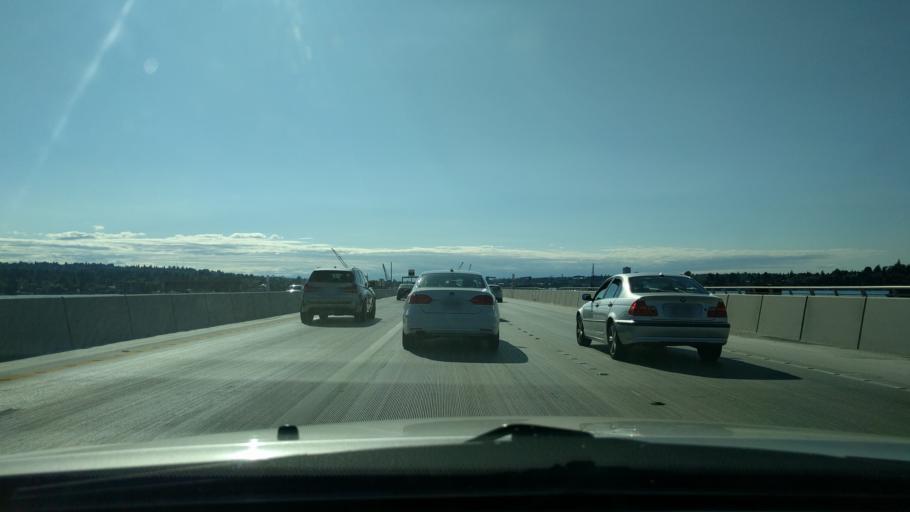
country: US
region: Washington
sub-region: King County
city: Medina
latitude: 47.6407
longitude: -122.2583
